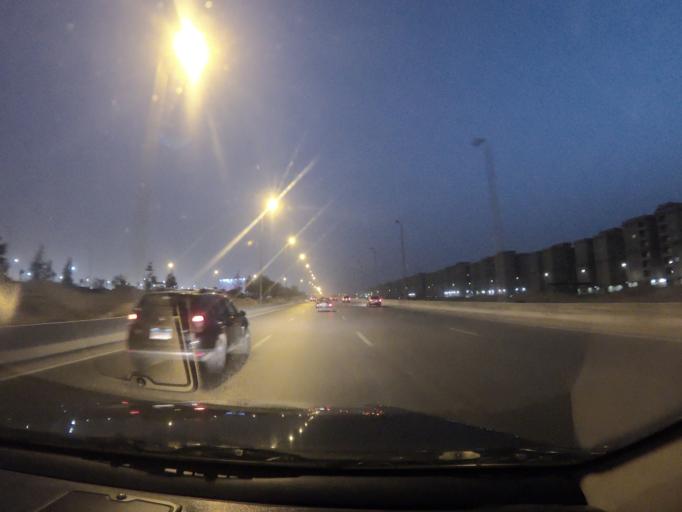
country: EG
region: Muhafazat al Qahirah
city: Cairo
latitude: 30.0442
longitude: 31.4039
